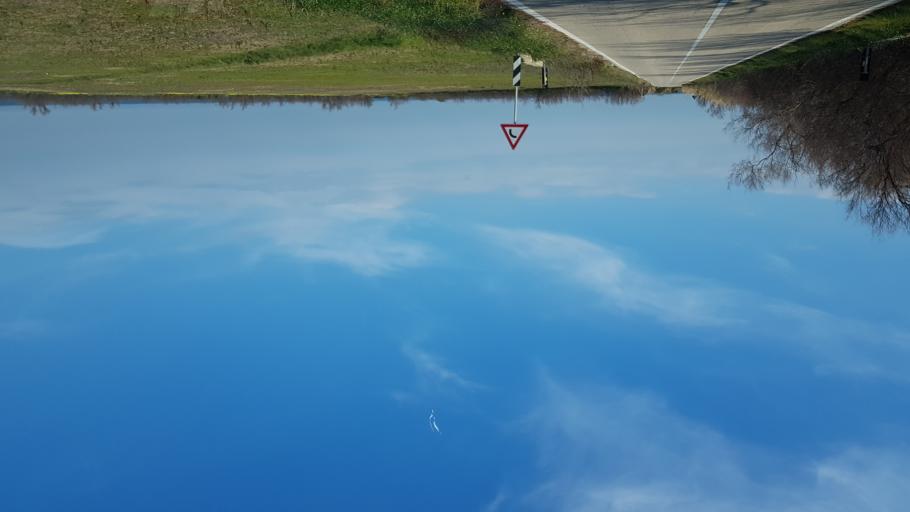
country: IT
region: Apulia
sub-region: Provincia di Brindisi
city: Brindisi
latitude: 40.6858
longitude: 17.8603
